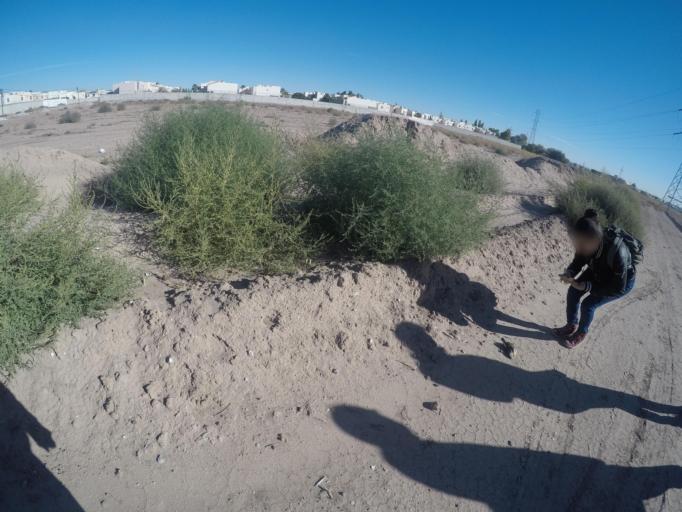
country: US
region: Texas
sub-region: El Paso County
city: Socorro
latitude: 31.6984
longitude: -106.3793
